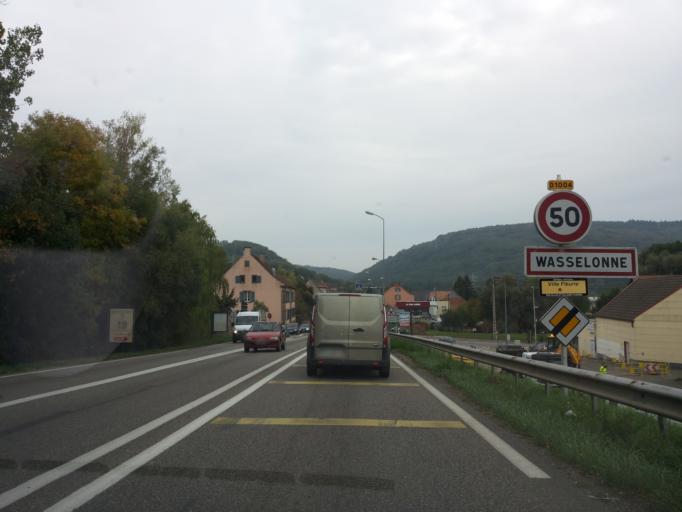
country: FR
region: Alsace
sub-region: Departement du Bas-Rhin
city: Wasselonne
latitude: 48.6397
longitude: 7.4540
